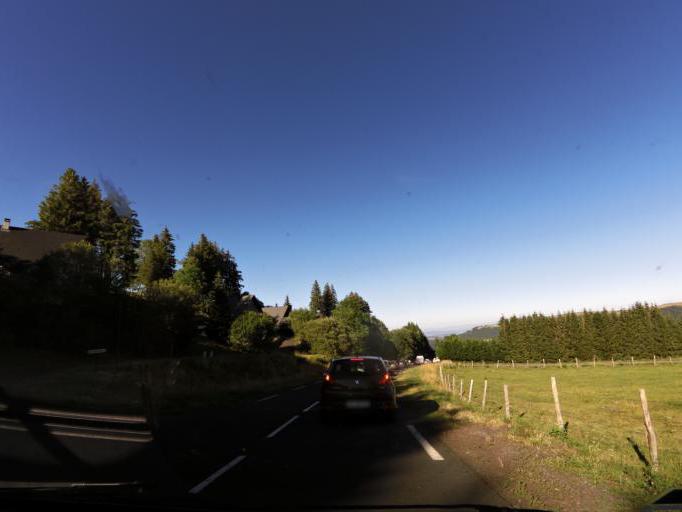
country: FR
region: Auvergne
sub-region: Departement du Puy-de-Dome
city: Mont-Dore
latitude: 45.5067
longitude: 2.9182
